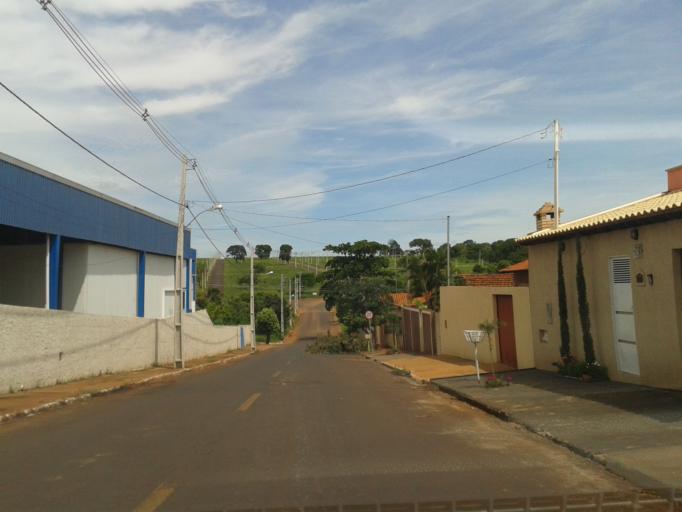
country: BR
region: Minas Gerais
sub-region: Santa Vitoria
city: Santa Vitoria
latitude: -18.8438
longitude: -50.1318
